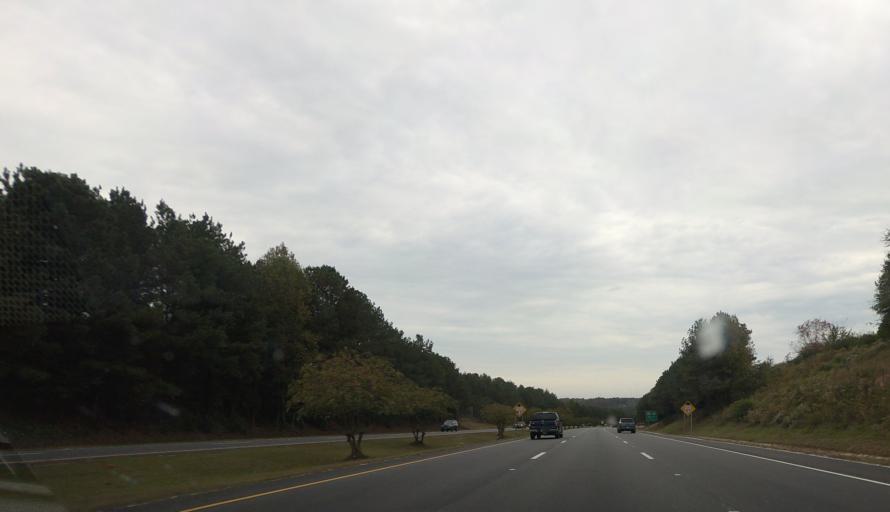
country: US
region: Alabama
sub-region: Russell County
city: Phenix City
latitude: 32.4950
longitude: -85.0229
